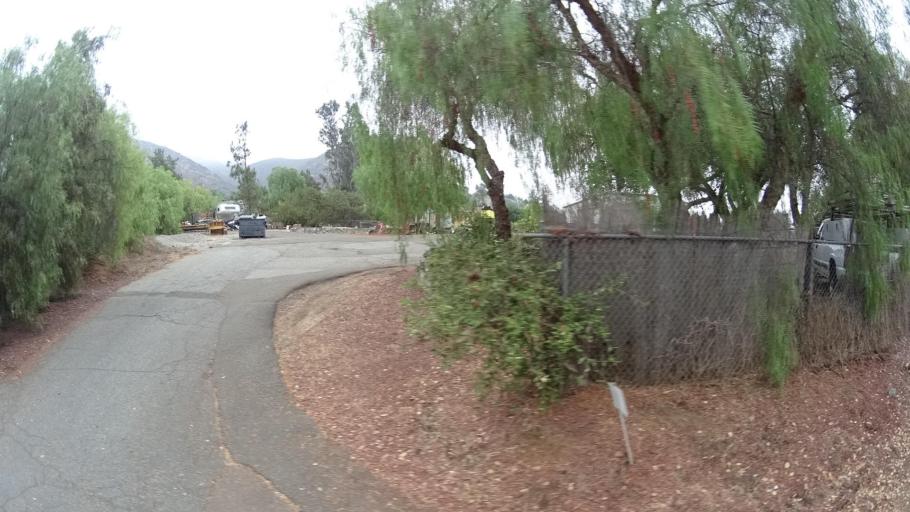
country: US
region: California
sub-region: San Diego County
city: Rainbow
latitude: 33.3714
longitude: -117.1616
